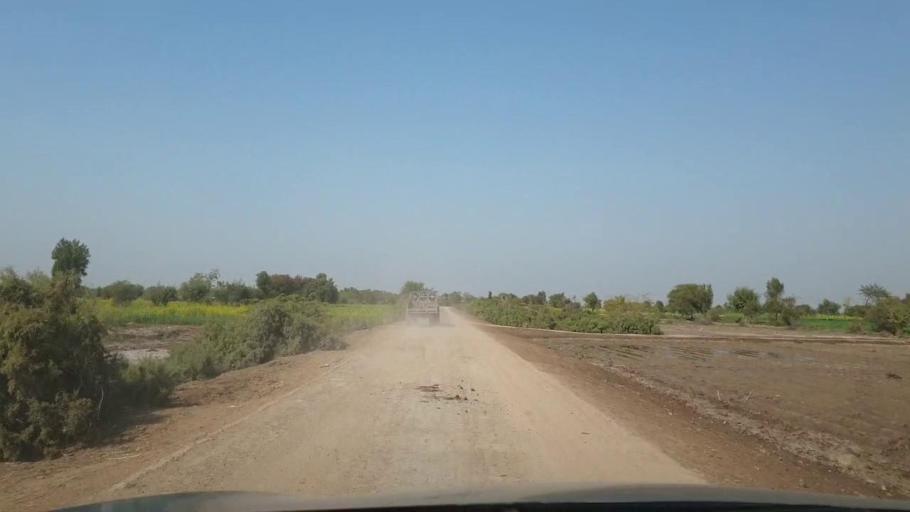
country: PK
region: Sindh
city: Berani
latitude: 25.6246
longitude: 68.8454
